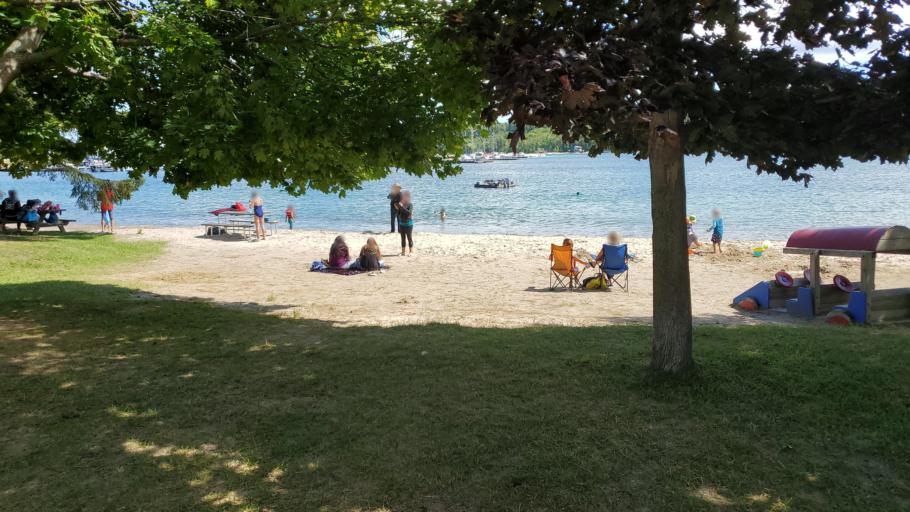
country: CA
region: Ontario
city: Tobermory
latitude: 44.9888
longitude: -81.2524
